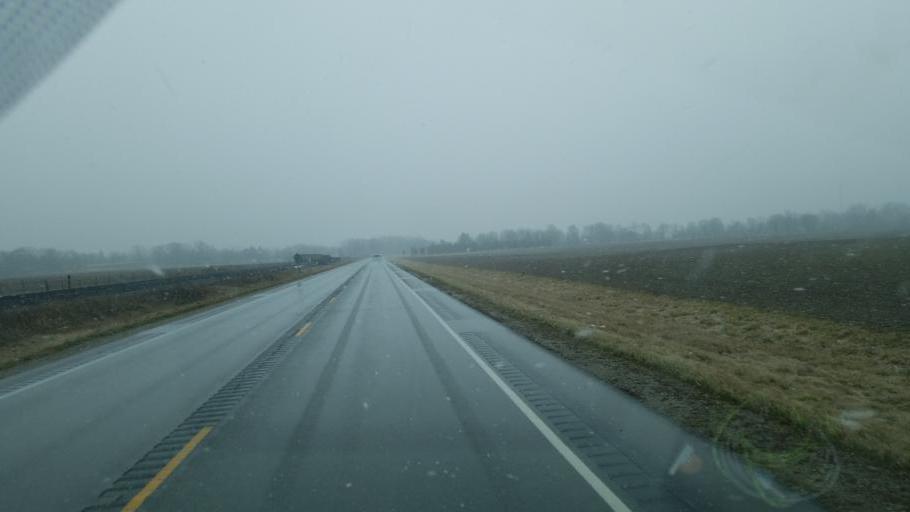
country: US
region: Indiana
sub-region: Wabash County
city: Mount Vernon
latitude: 40.6807
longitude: -85.7325
